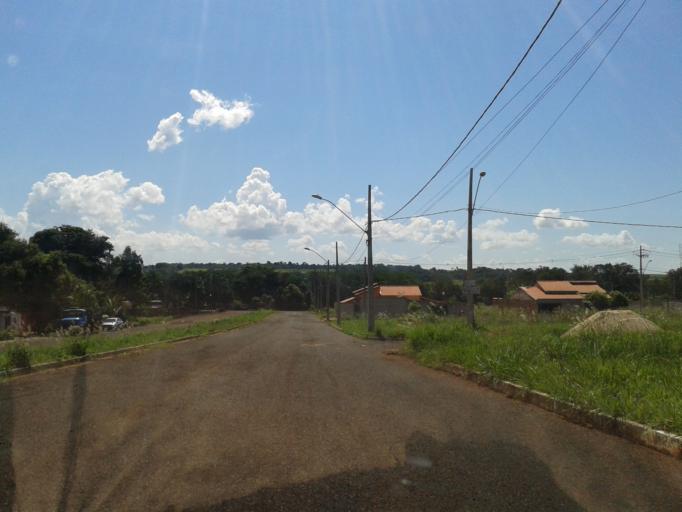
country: BR
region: Goias
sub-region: Itumbiara
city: Itumbiara
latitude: -18.4231
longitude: -49.1858
